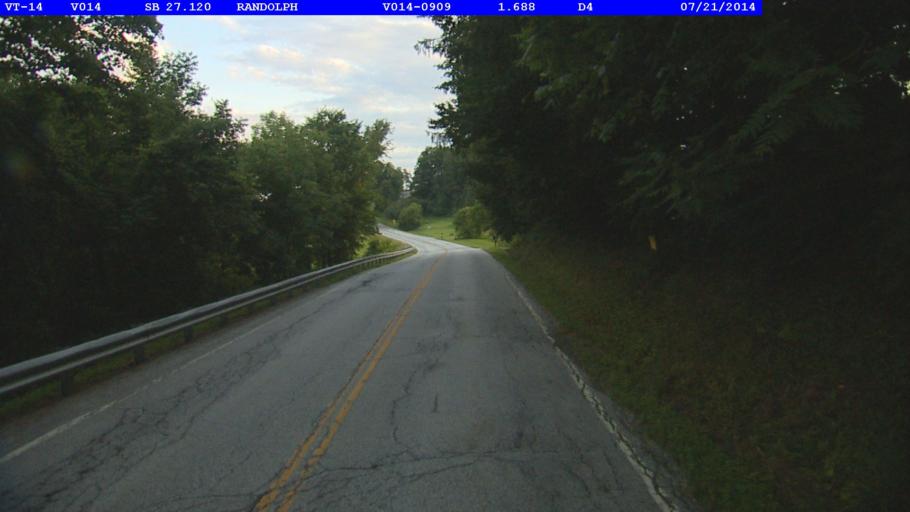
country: US
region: Vermont
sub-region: Orange County
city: Randolph
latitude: 43.8982
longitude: -72.5729
